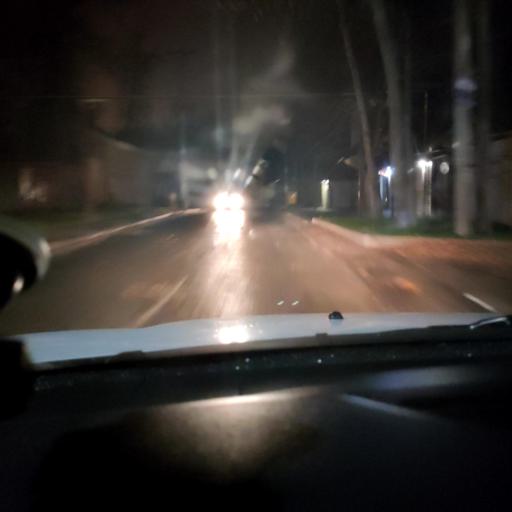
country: RU
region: Samara
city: Samara
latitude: 53.2917
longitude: 50.1999
